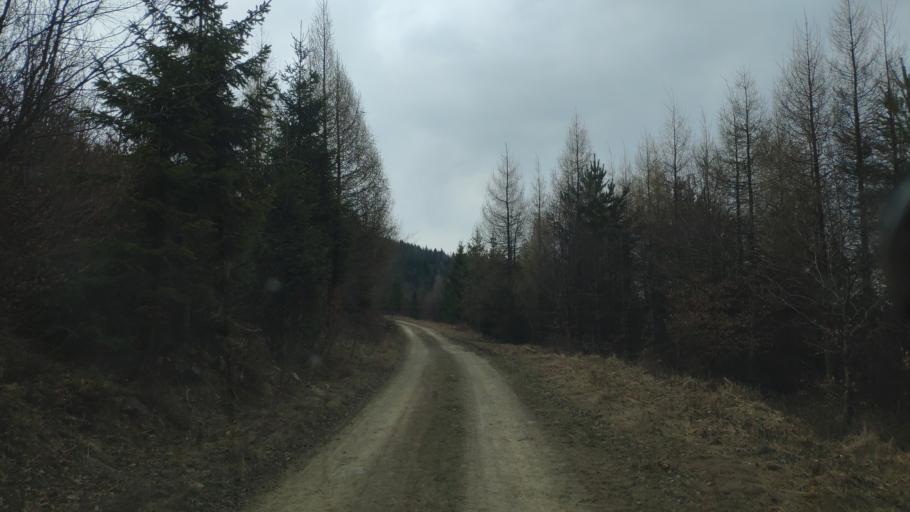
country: SK
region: Kosicky
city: Gelnica
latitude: 48.7600
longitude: 21.0363
